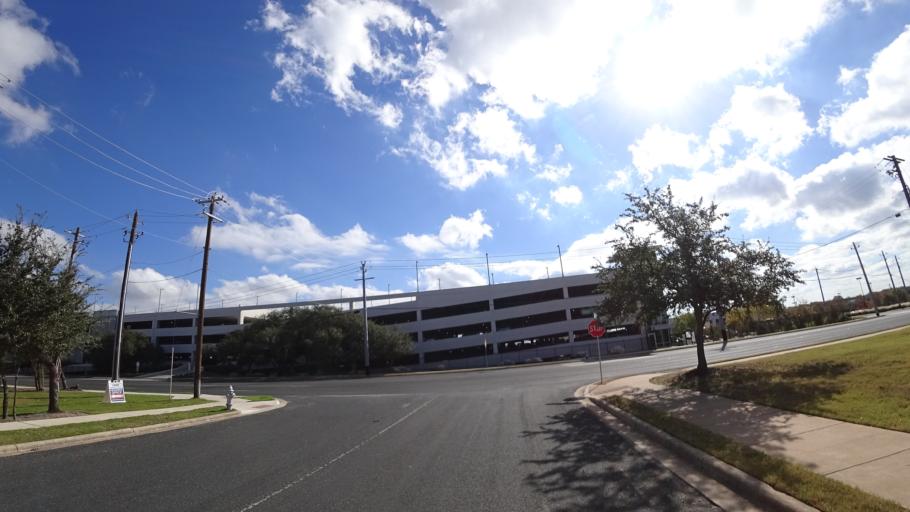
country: US
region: Texas
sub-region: Williamson County
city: Jollyville
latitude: 30.4347
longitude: -97.7388
